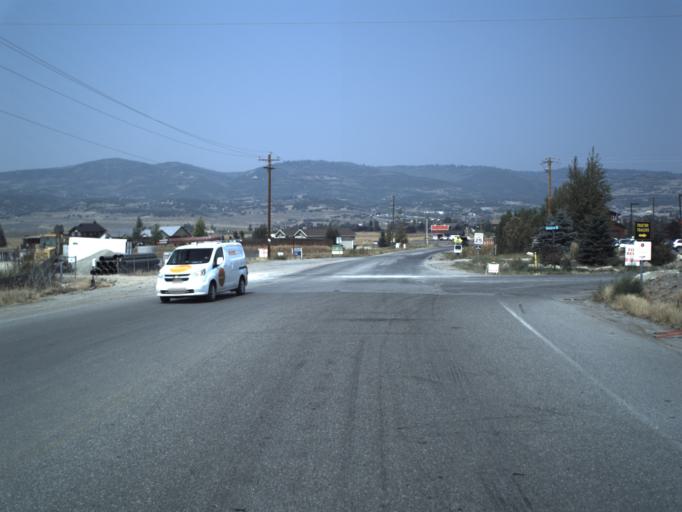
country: US
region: Utah
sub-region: Summit County
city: Snyderville
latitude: 40.7340
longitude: -111.4993
